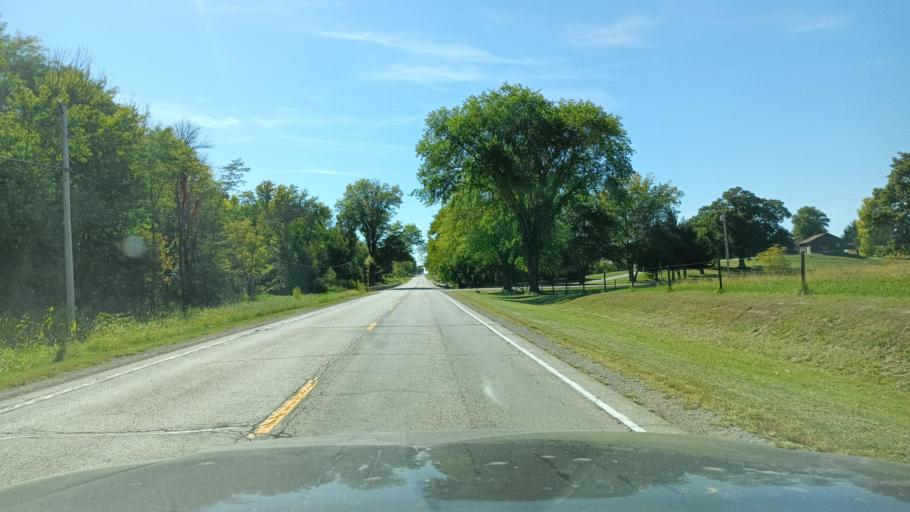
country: US
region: Illinois
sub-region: De Witt County
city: Farmer City
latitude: 40.2289
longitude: -88.6830
